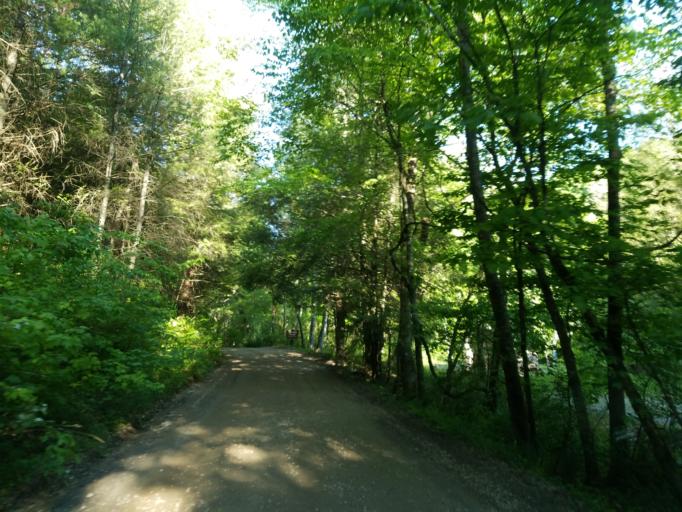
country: US
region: Georgia
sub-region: Lumpkin County
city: Dahlonega
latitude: 34.7012
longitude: -84.1491
